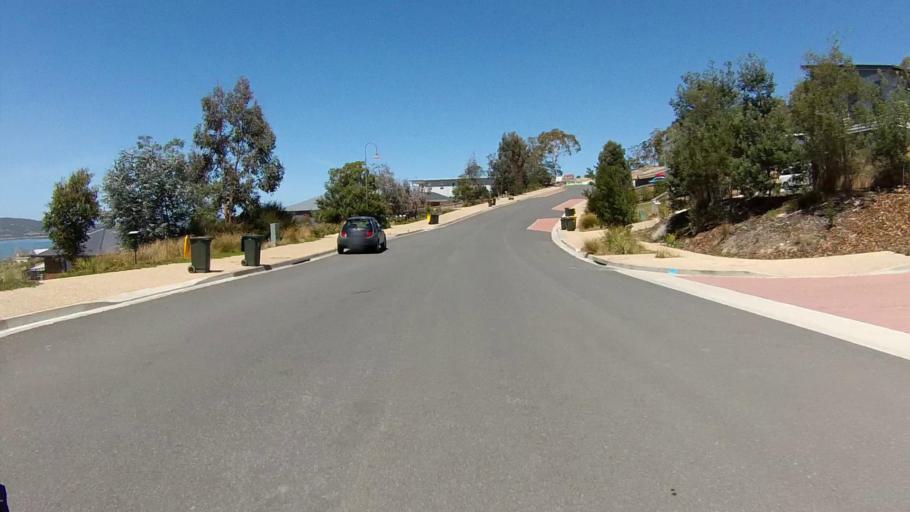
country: AU
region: Tasmania
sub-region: Clarence
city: Rokeby
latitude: -42.9071
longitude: 147.4289
